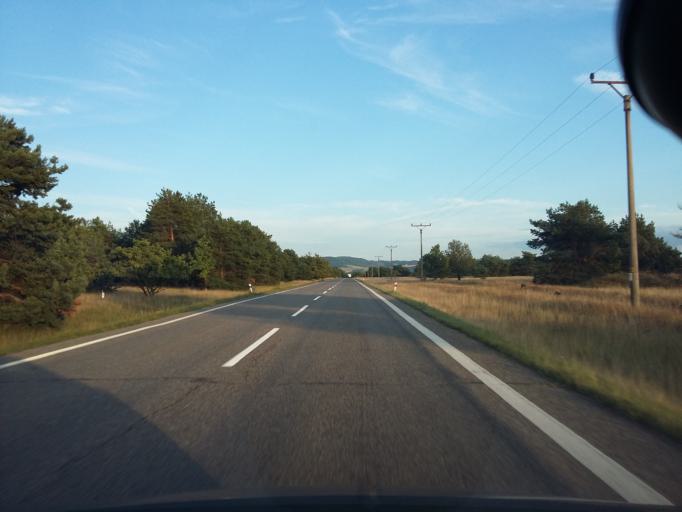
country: SK
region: Bratislavsky
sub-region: Okres Malacky
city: Malacky
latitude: 48.4160
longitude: 17.0617
